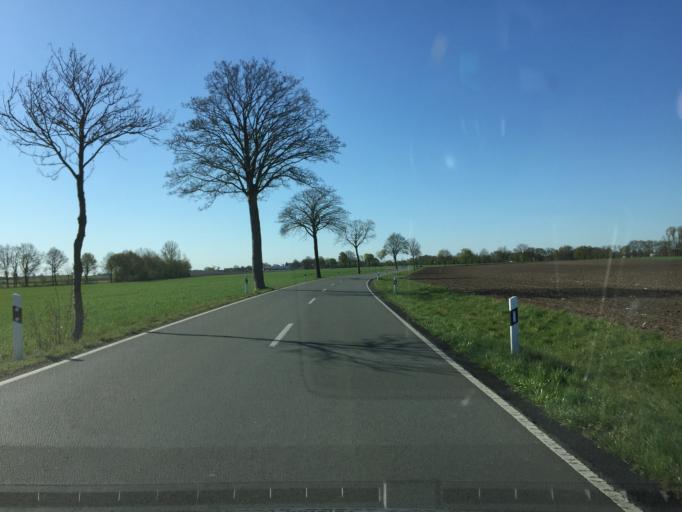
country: DE
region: Lower Saxony
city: Varrel
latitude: 52.6354
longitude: 8.7380
